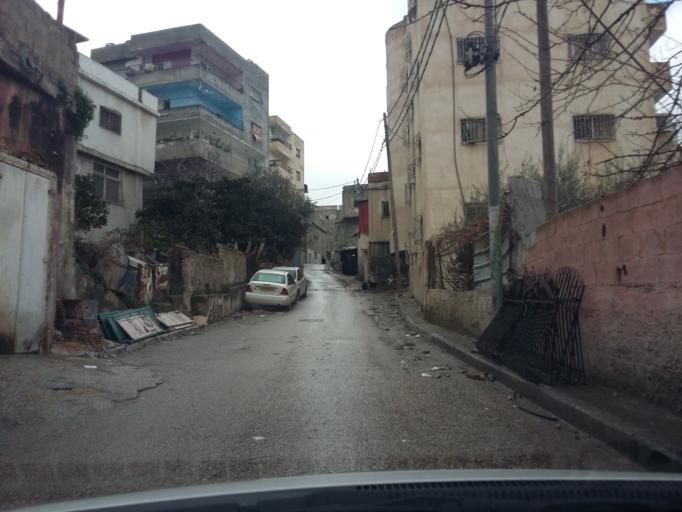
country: PS
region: West Bank
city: `Anata
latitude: 31.8103
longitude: 35.2499
